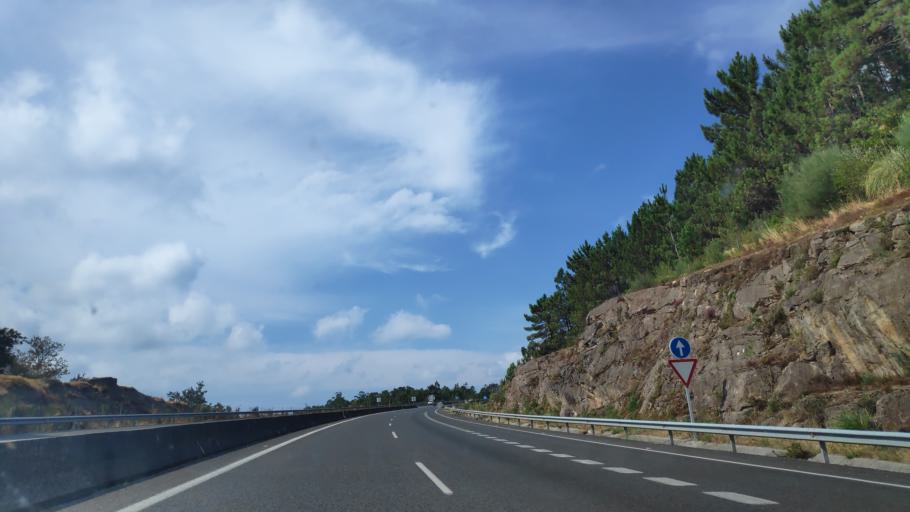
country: ES
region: Galicia
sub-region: Provincia de Pontevedra
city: Catoira
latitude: 42.7049
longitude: -8.7308
